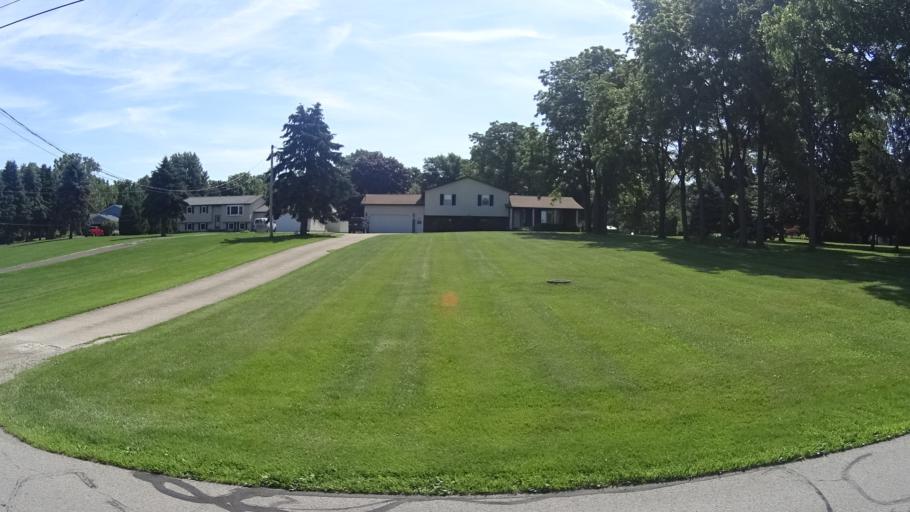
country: US
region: Ohio
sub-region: Erie County
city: Huron
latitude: 41.3820
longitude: -82.4585
